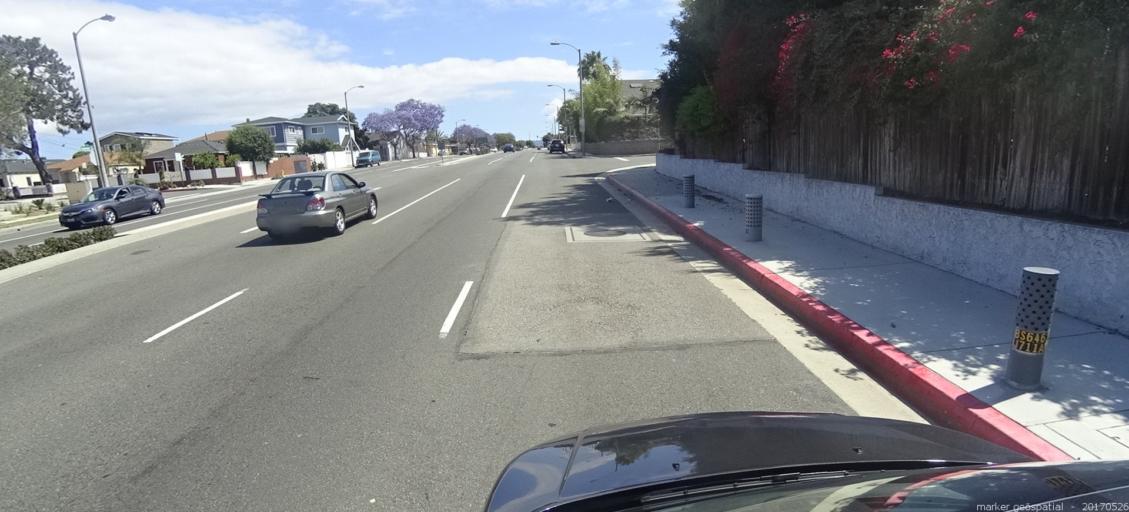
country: US
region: California
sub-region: Los Angeles County
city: Lawndale
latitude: 33.8831
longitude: -118.3614
